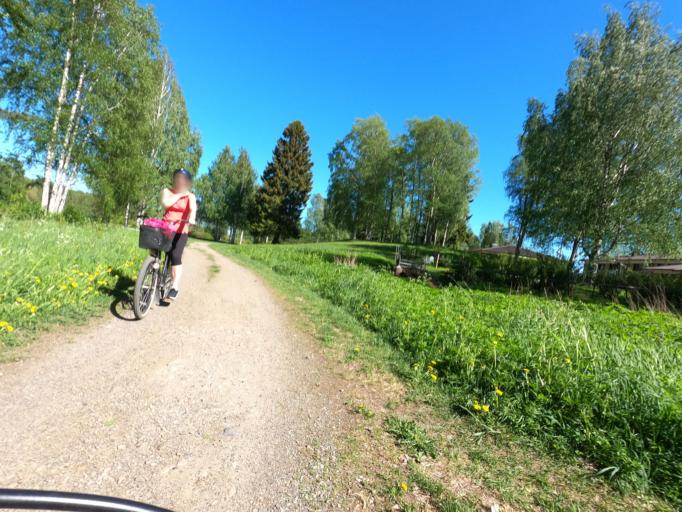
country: FI
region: North Karelia
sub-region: Joensuu
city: Joensuu
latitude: 62.6076
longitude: 29.8044
